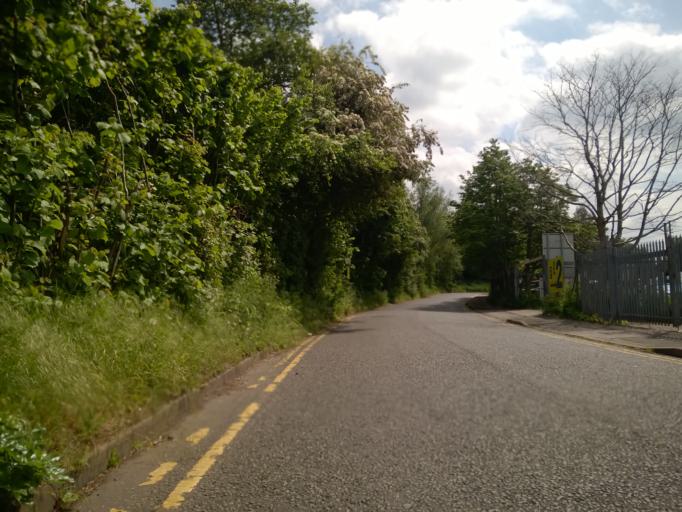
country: GB
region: England
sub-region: City of Leicester
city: Leicester
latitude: 52.6348
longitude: -1.1438
